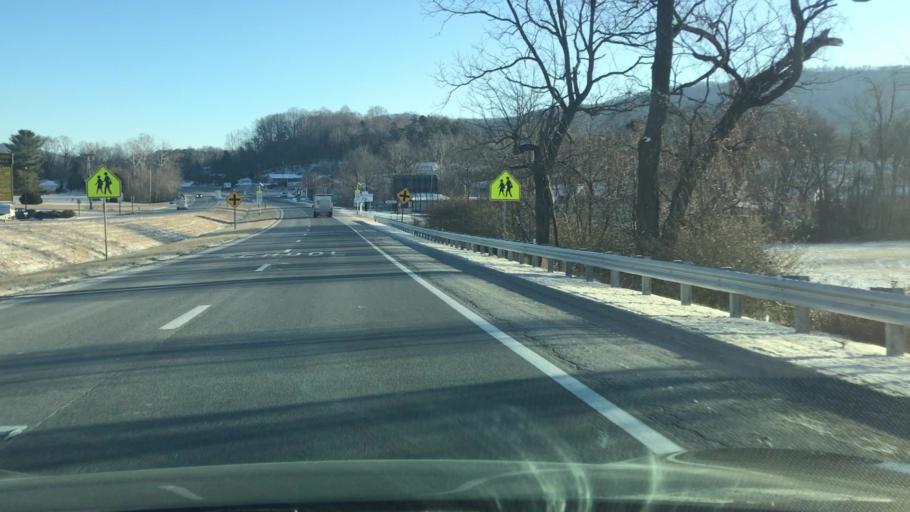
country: US
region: Virginia
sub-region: Botetourt County
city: Blue Ridge
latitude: 37.3641
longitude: -79.8205
